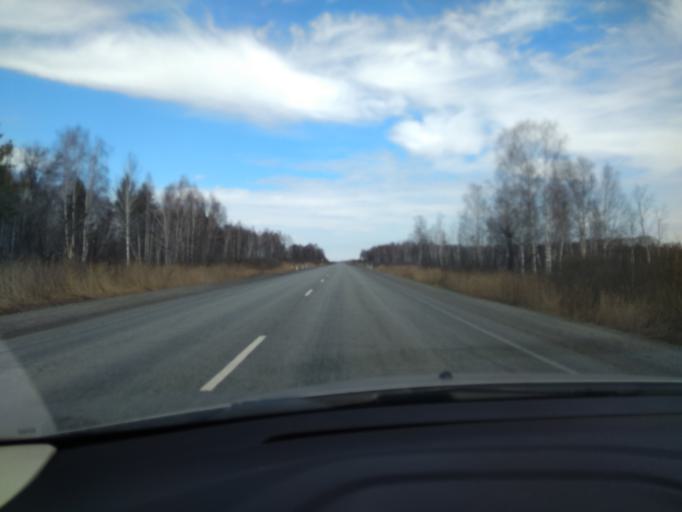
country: RU
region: Sverdlovsk
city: Pyshma
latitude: 57.0060
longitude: 63.3320
